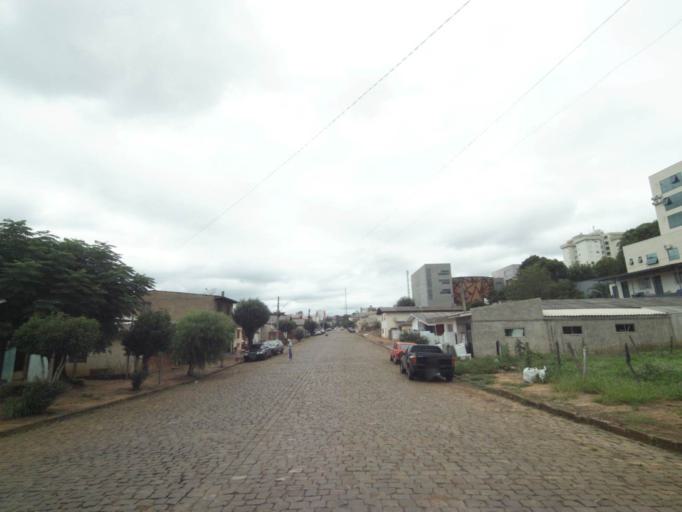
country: BR
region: Rio Grande do Sul
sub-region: Lagoa Vermelha
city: Lagoa Vermelha
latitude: -28.2068
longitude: -51.5282
